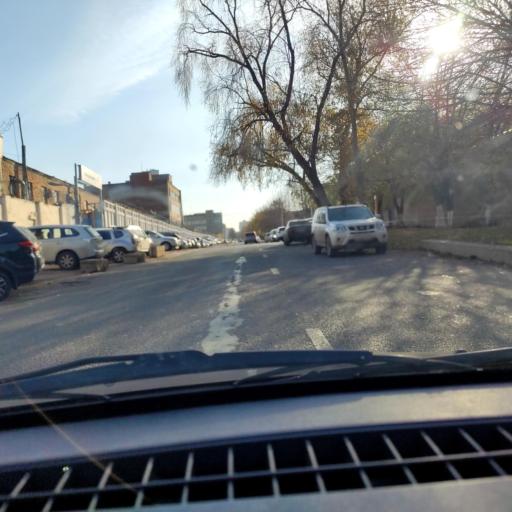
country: RU
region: Bashkortostan
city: Ufa
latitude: 54.7374
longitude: 55.9370
